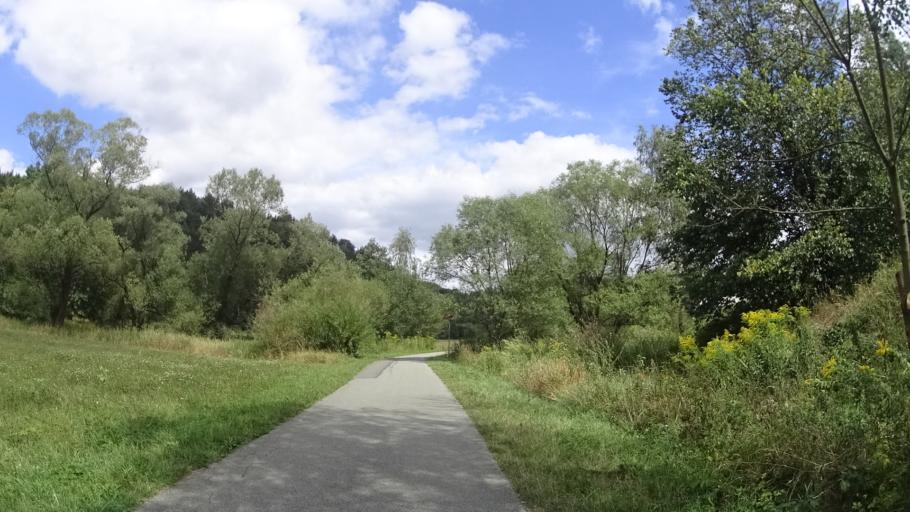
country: CZ
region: Pardubicky
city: Brandys nad Orlici
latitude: 49.9893
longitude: 16.3341
